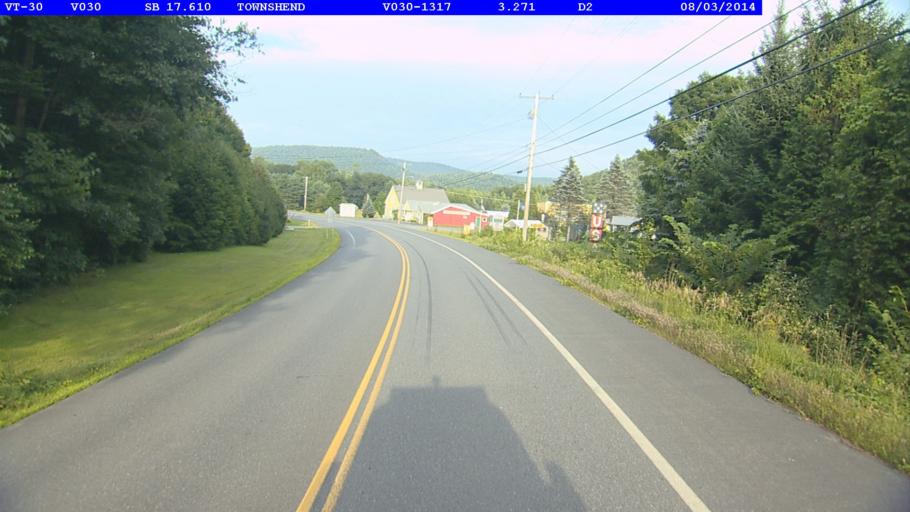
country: US
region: Vermont
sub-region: Windham County
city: Newfane
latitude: 43.0453
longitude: -72.6910
